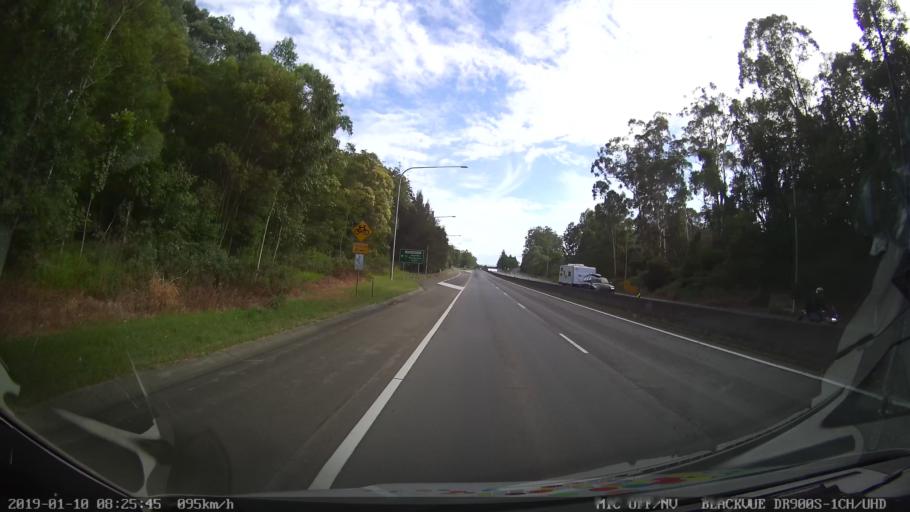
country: AU
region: New South Wales
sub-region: Coffs Harbour
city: Bonville
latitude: -30.4296
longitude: 153.0191
